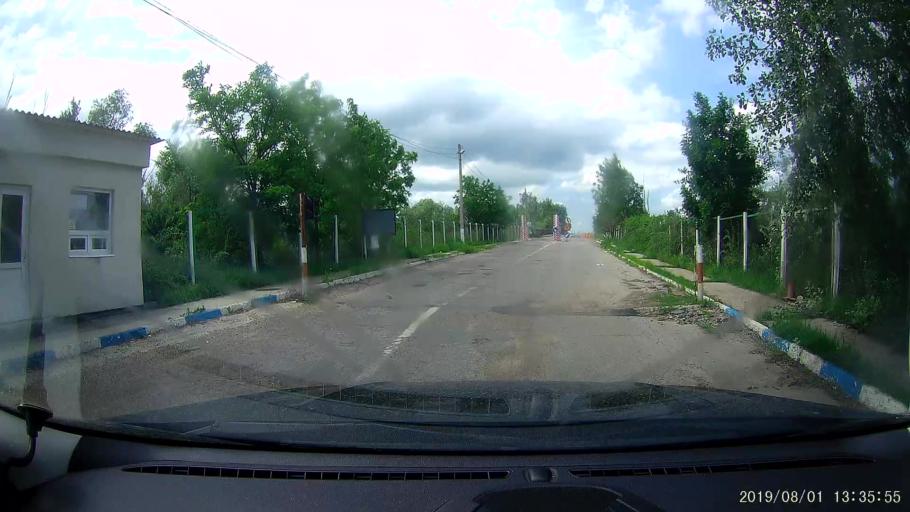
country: RO
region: Galati
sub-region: Comuna Oancea
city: Oancea
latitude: 45.9168
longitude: 28.1232
